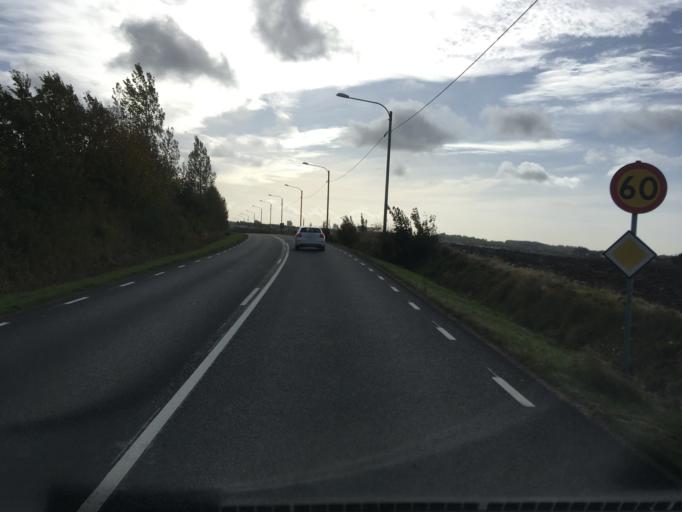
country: SE
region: Skane
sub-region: Lunds Kommun
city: Lund
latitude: 55.7373
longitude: 13.1983
